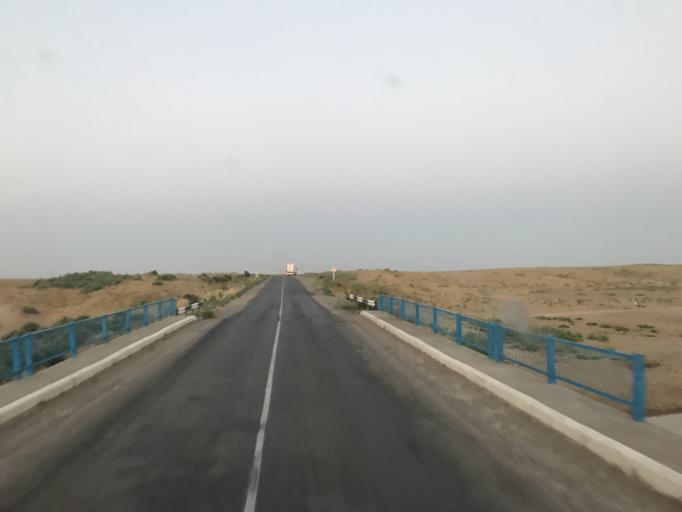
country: UZ
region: Toshkent
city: Chinoz
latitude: 41.1989
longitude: 68.6103
